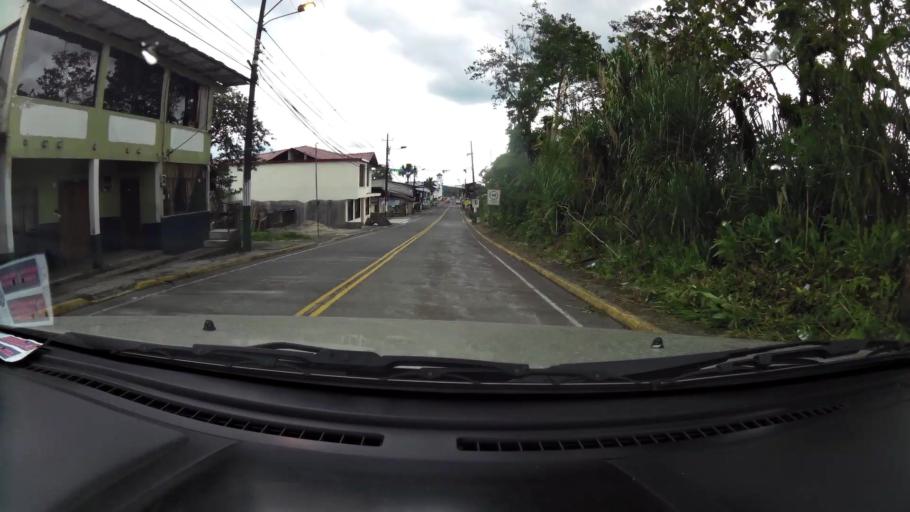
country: EC
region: Pastaza
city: Puyo
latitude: -1.4600
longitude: -78.1156
